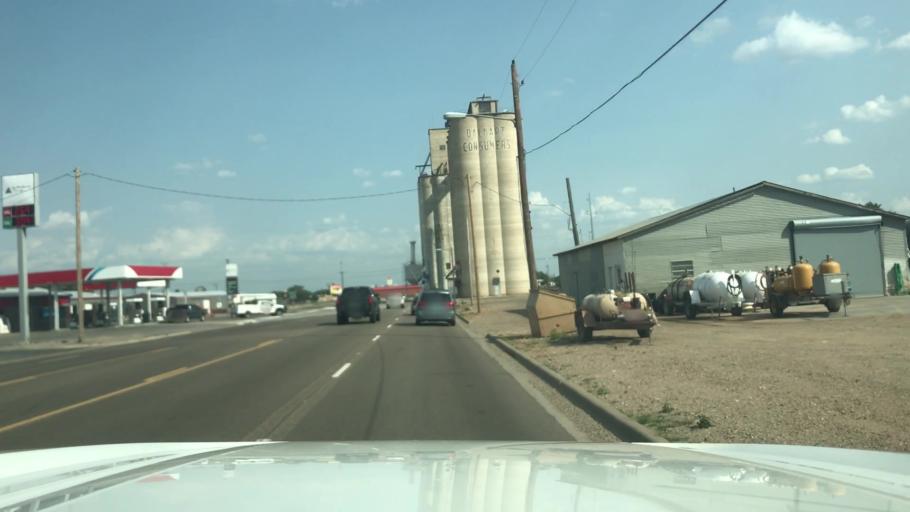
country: US
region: Texas
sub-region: Dallam County
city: Dalhart
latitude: 36.0687
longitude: -102.5269
